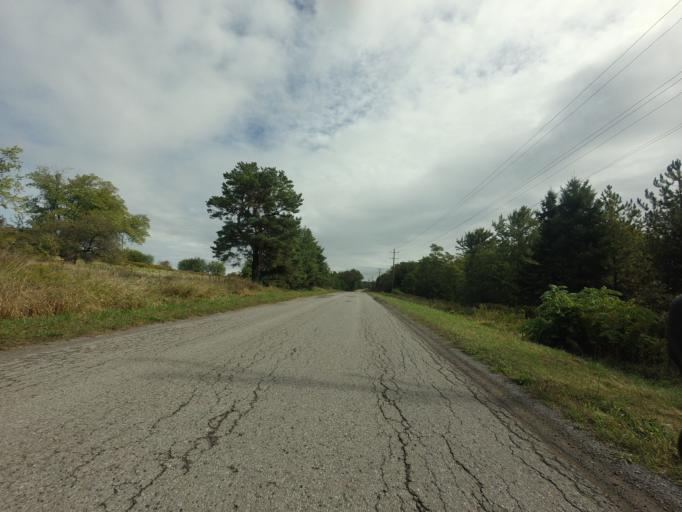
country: CA
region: Ontario
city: Cobourg
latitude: 43.9287
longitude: -78.3939
